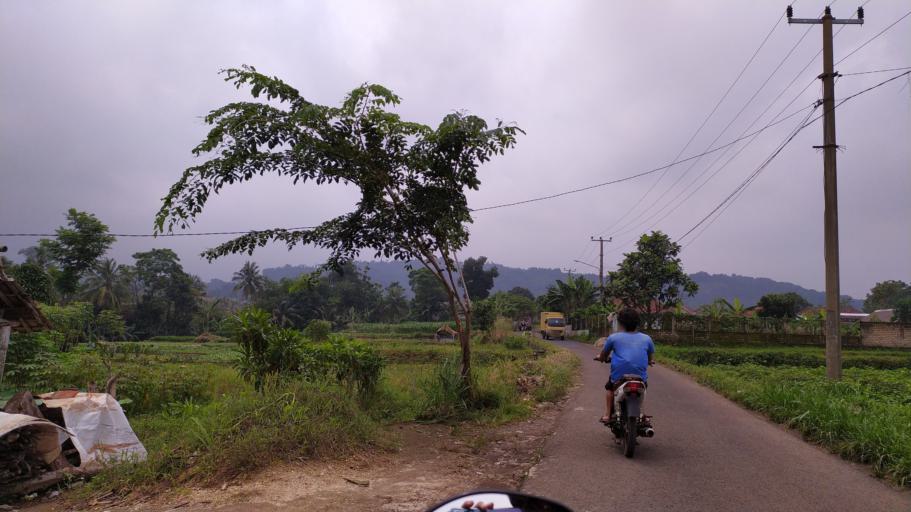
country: ID
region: West Java
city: Ciampea
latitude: -6.6139
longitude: 106.7092
